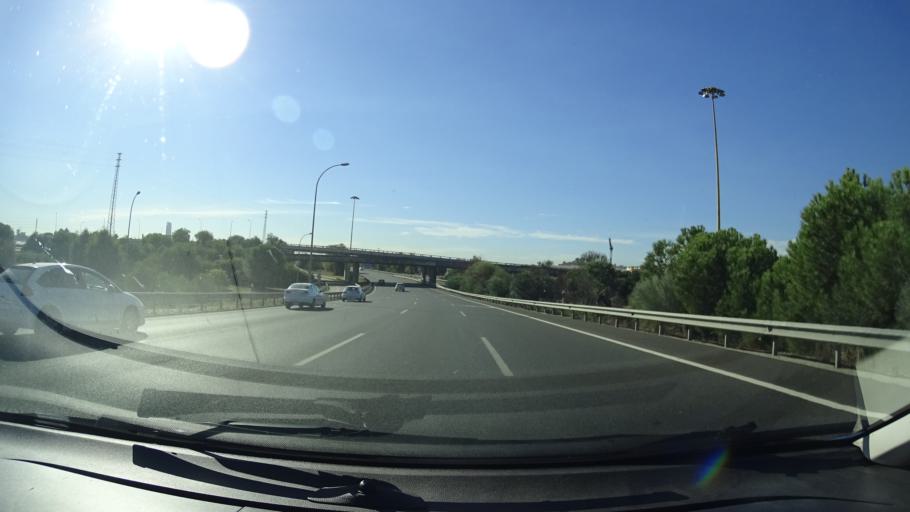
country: ES
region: Andalusia
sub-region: Provincia de Sevilla
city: Camas
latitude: 37.4108
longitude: -6.0341
